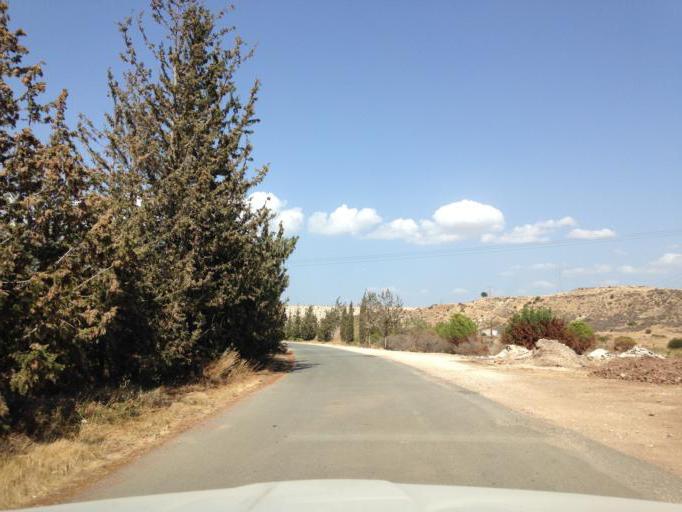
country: CY
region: Pafos
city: Mesogi
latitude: 34.7163
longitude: 32.5489
